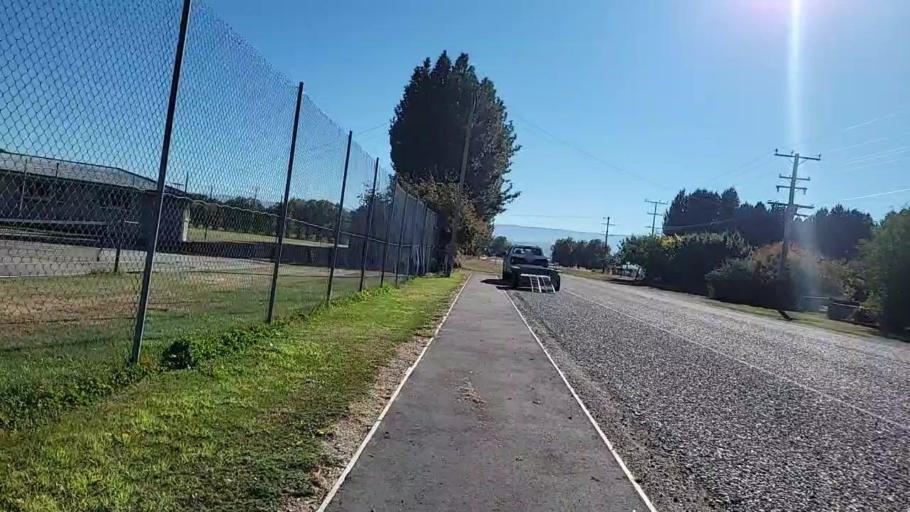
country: NZ
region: Otago
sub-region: Queenstown-Lakes District
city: Wanaka
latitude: -45.0031
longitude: 169.9167
